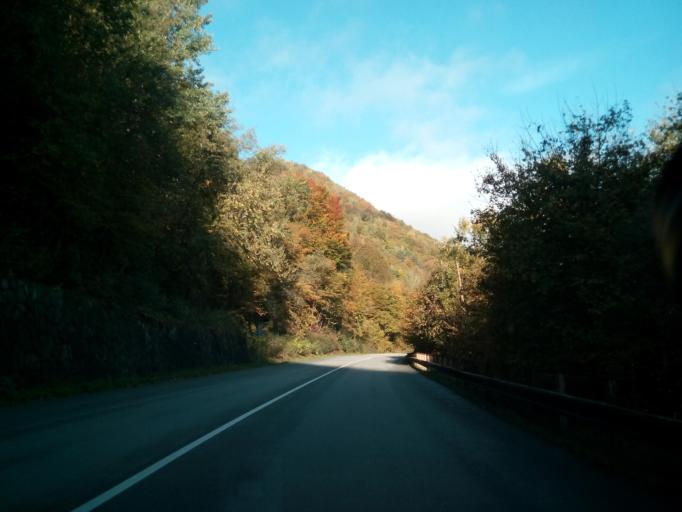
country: SK
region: Kosicky
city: Gelnica
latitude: 48.8890
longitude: 20.9991
